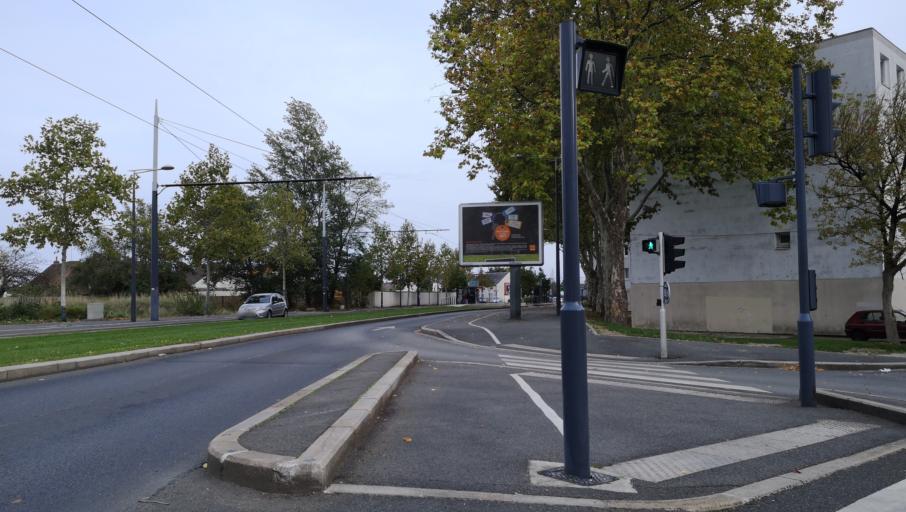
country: FR
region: Centre
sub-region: Departement du Loiret
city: Saint-Jean-le-Blanc
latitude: 47.9108
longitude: 1.9317
